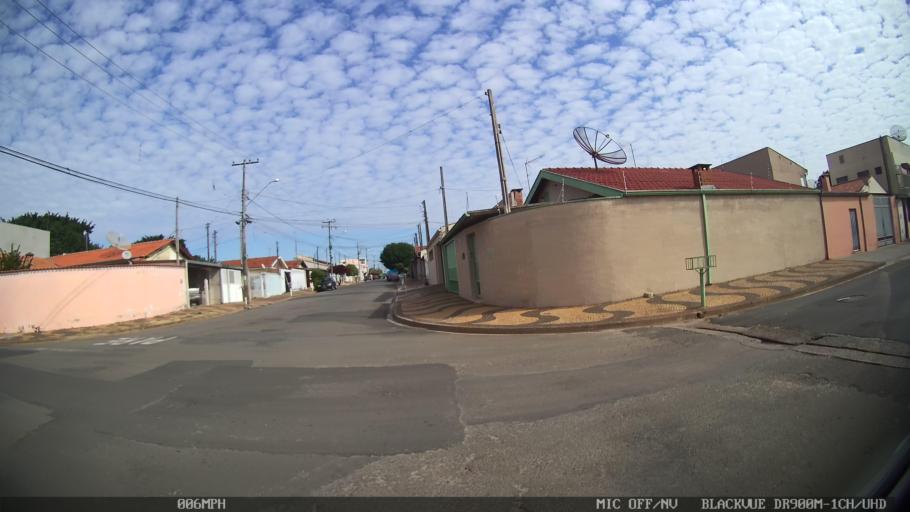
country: BR
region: Sao Paulo
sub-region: Santa Barbara D'Oeste
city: Santa Barbara d'Oeste
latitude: -22.7685
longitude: -47.3917
